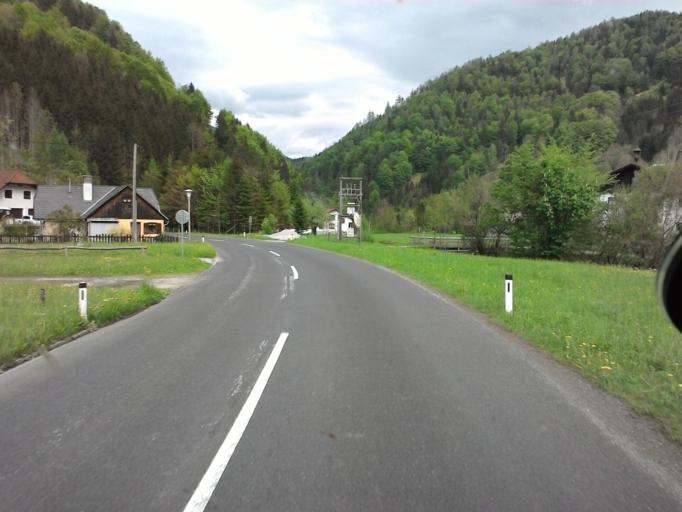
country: AT
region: Styria
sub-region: Politischer Bezirk Liezen
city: Sankt Gallen
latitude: 47.7171
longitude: 14.5668
